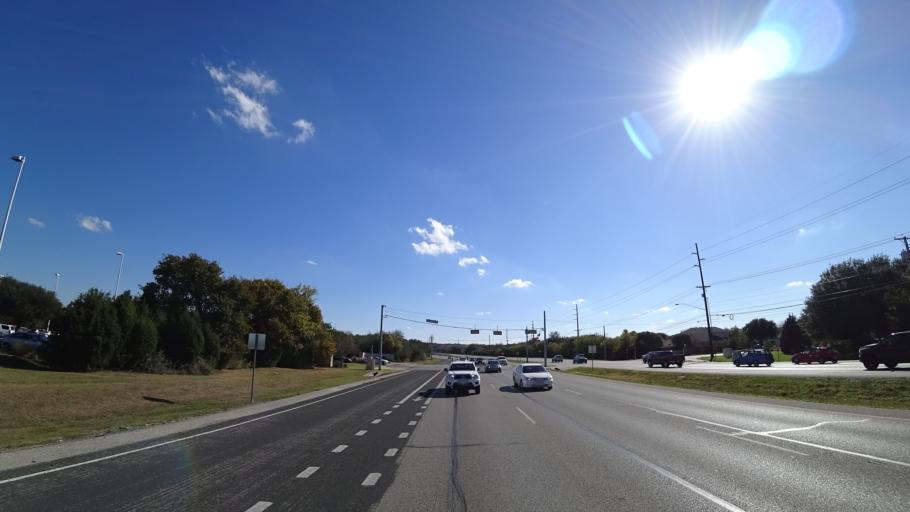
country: US
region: Texas
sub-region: Williamson County
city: Jollyville
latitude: 30.4565
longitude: -97.7529
